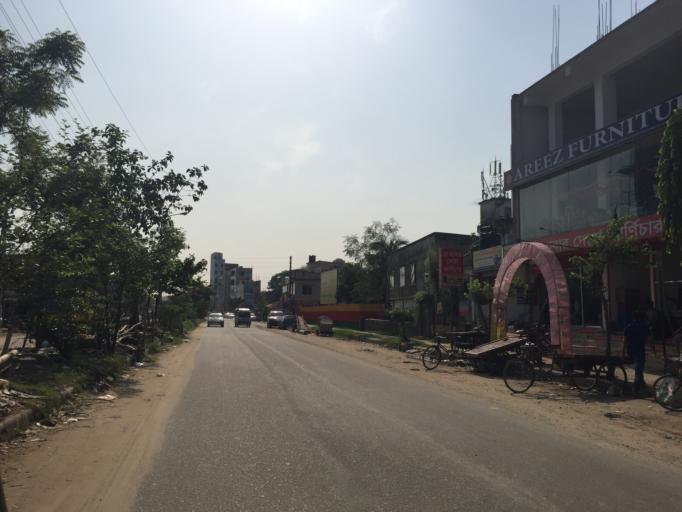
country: BD
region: Dhaka
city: Paltan
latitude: 23.7987
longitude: 90.4340
